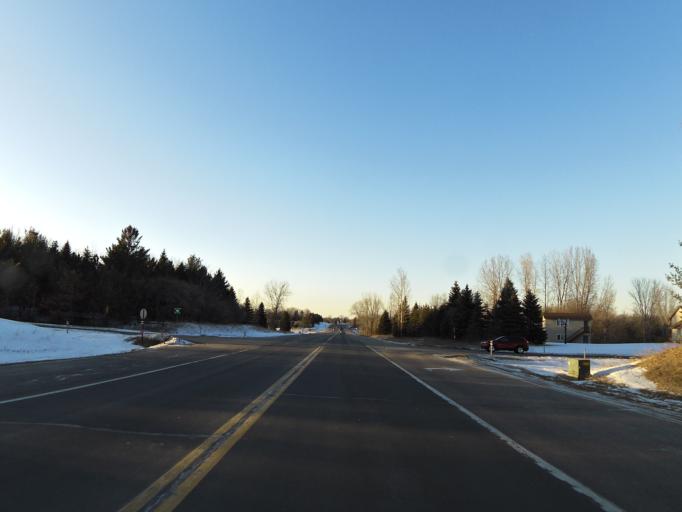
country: US
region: Minnesota
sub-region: Washington County
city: Lake Elmo
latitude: 44.9744
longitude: -92.8560
